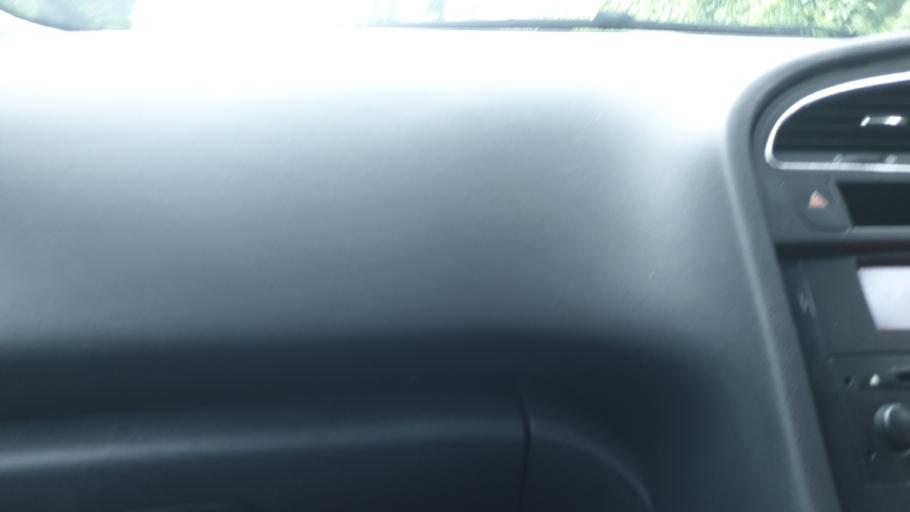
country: IE
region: Munster
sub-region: Ciarrai
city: Tralee
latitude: 52.2538
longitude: -9.6432
